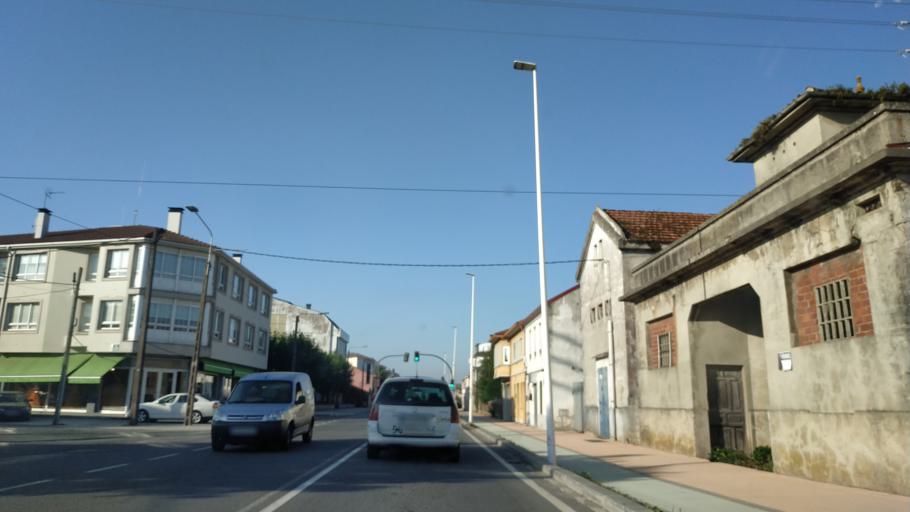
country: ES
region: Galicia
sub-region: Provincia da Coruna
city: Carballo
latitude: 43.2261
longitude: -8.6784
